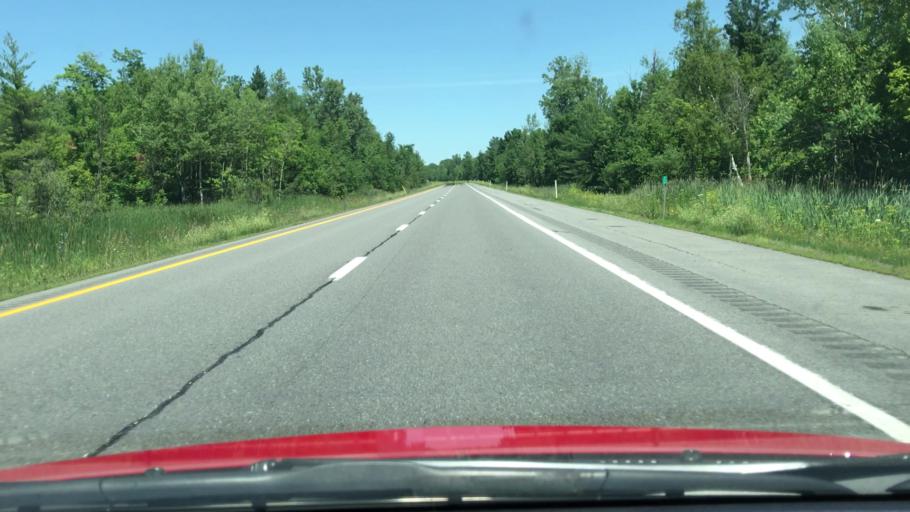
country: US
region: New York
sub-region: Clinton County
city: Champlain
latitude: 44.9104
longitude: -73.4499
